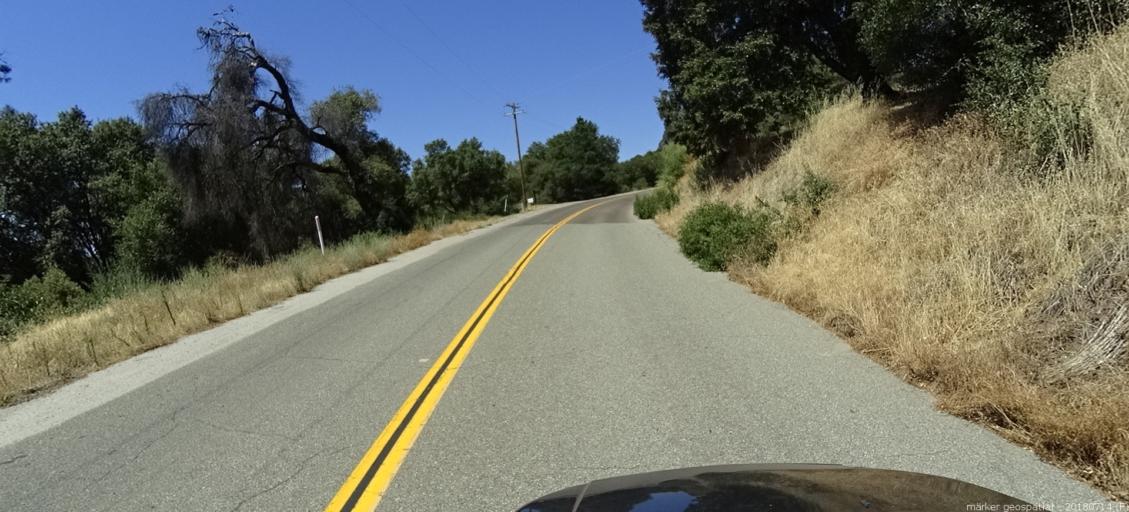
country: US
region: California
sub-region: Madera County
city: Oakhurst
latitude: 37.3687
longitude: -119.6359
